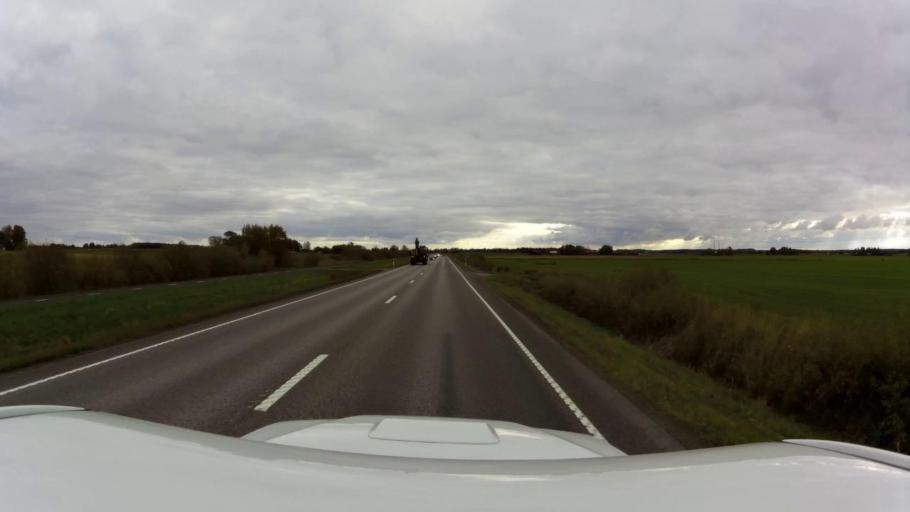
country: SE
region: OEstergoetland
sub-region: Linkopings Kommun
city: Berg
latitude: 58.4594
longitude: 15.5444
